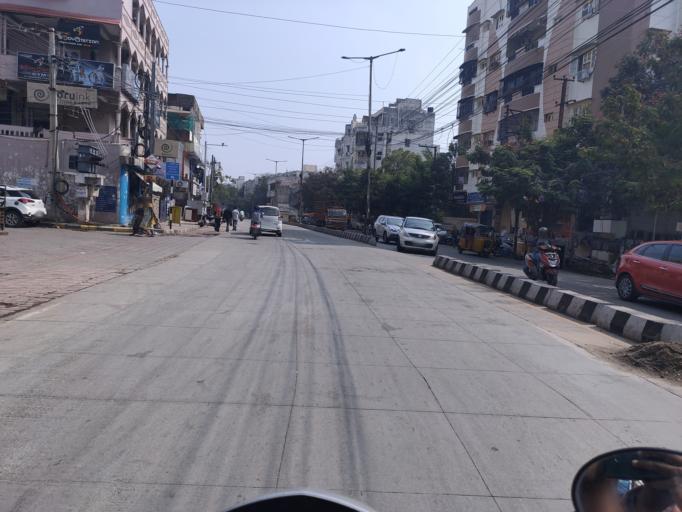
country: IN
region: Telangana
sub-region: Hyderabad
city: Malkajgiri
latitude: 17.4401
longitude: 78.4833
